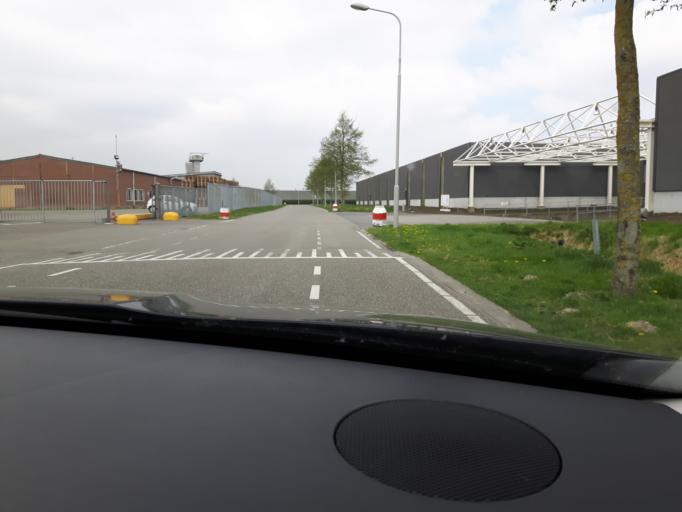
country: NL
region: Zeeland
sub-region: Gemeente Reimerswaal
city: Yerseke
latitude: 51.4722
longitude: 3.9735
